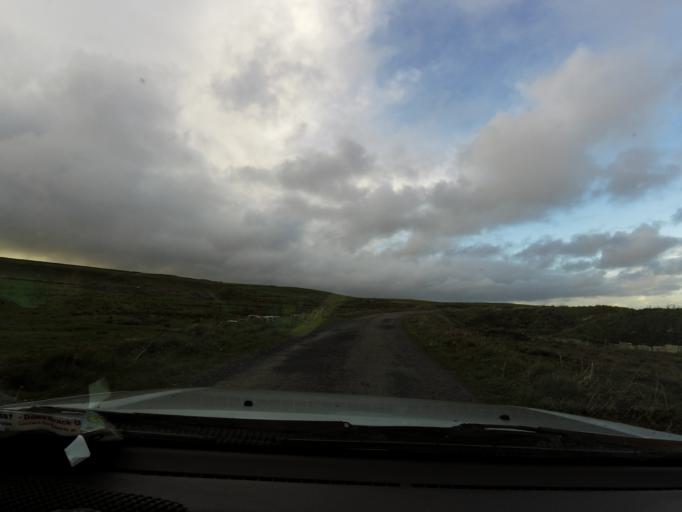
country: IE
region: Munster
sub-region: An Clar
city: Kilrush
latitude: 52.9575
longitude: -9.4359
